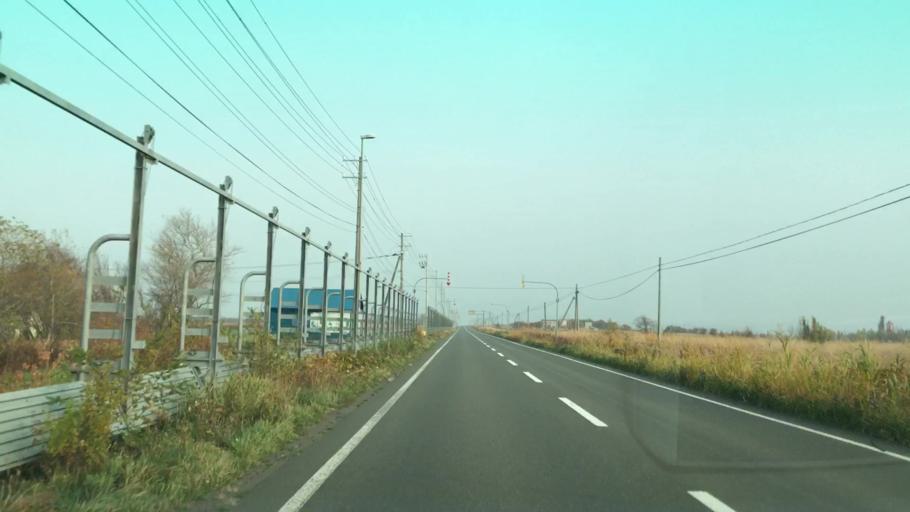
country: JP
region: Hokkaido
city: Ishikari
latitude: 43.2927
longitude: 141.4105
